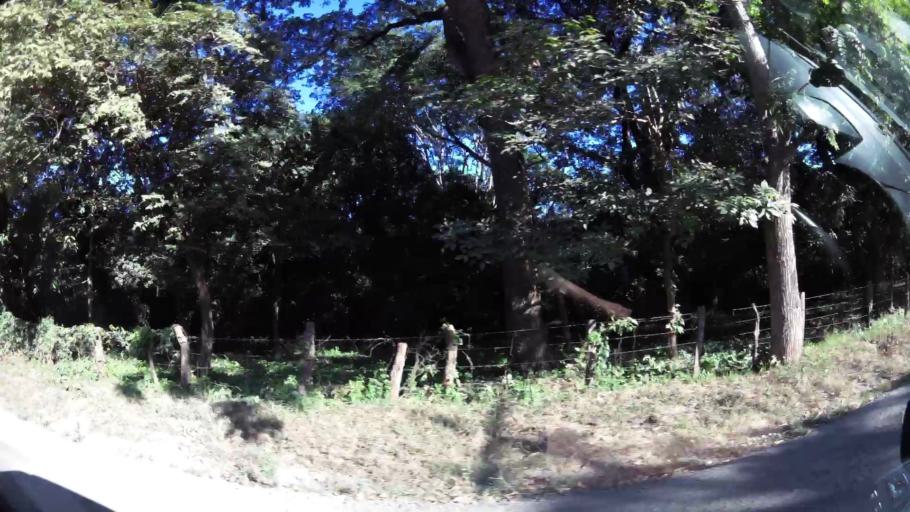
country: CR
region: Guanacaste
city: Sardinal
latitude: 10.4816
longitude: -85.5997
